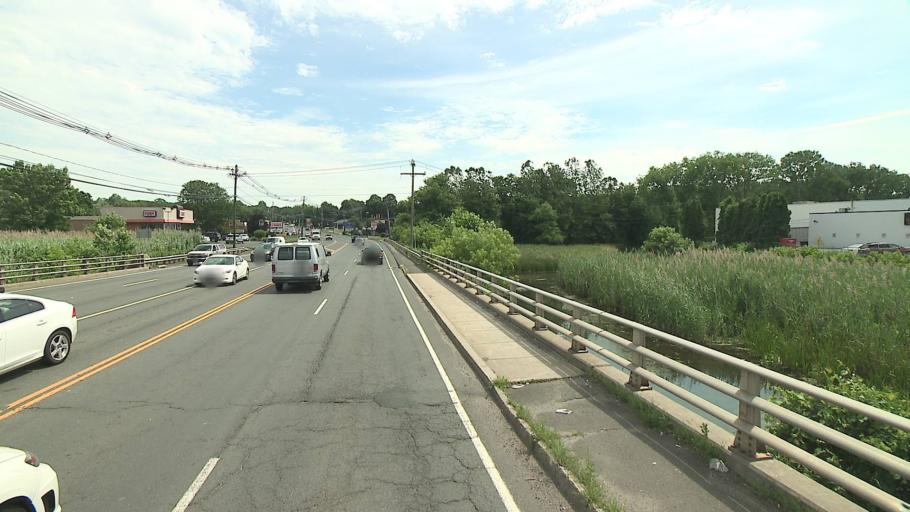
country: US
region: Connecticut
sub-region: Fairfield County
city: Bethel
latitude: 41.4095
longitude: -73.4144
